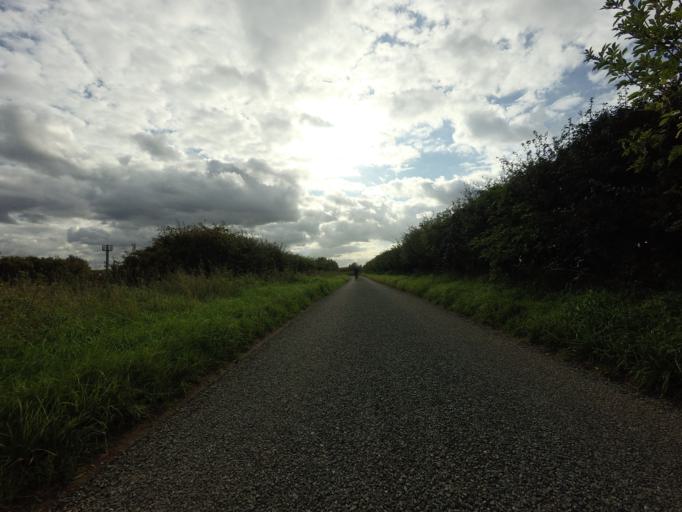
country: GB
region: England
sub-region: Norfolk
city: Dersingham
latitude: 52.8511
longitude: 0.5124
